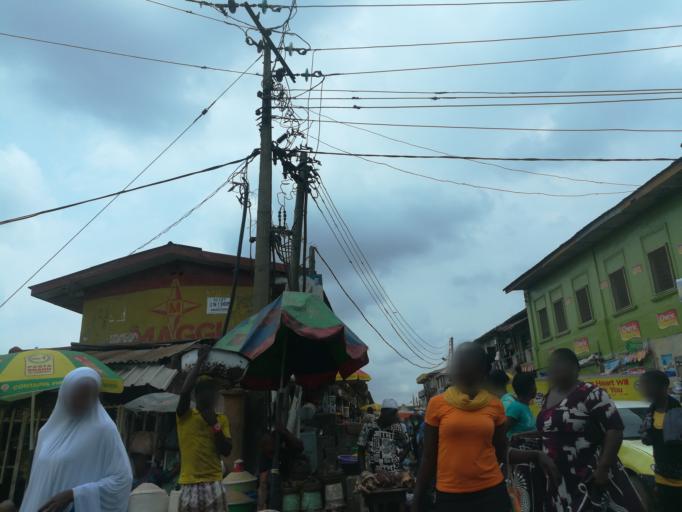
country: NG
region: Lagos
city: Agege
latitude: 6.6208
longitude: 3.3253
